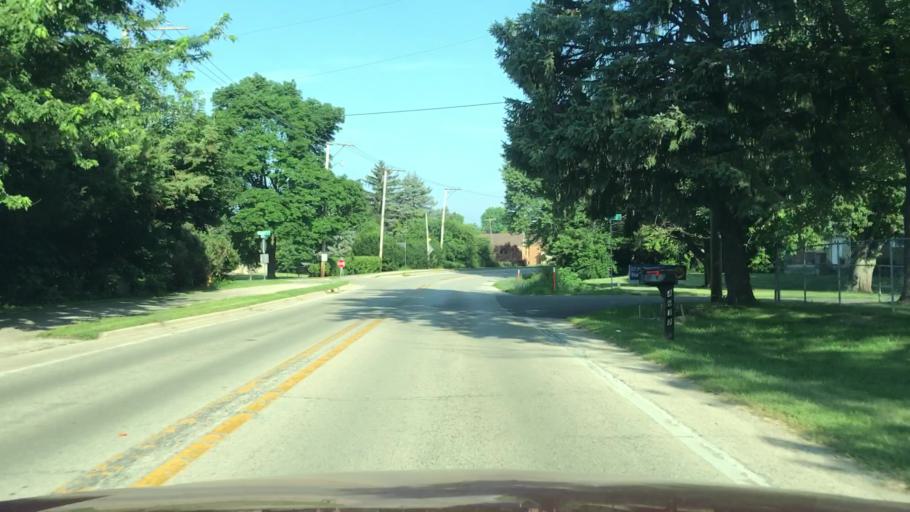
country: US
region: Illinois
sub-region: Winnebago County
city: Cherry Valley
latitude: 42.2478
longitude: -89.0223
